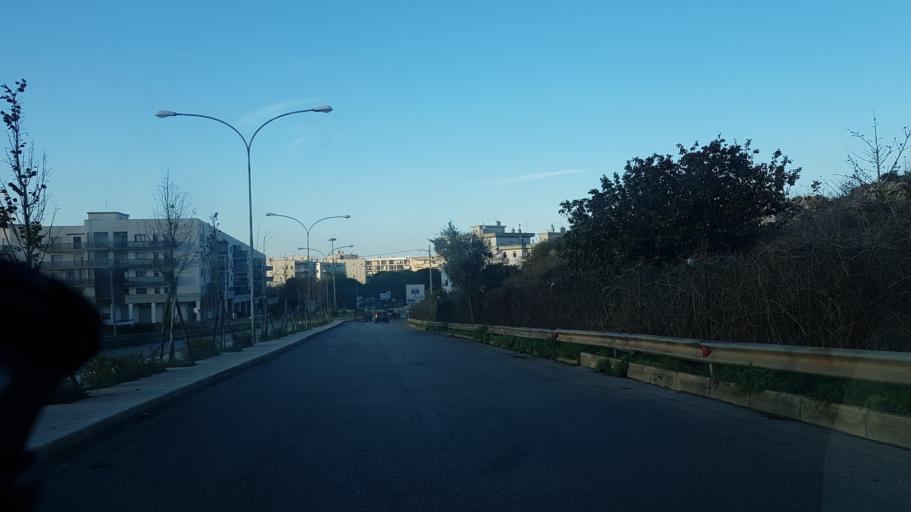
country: IT
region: Apulia
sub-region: Provincia di Brindisi
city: Ostuni
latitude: 40.7242
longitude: 17.5718
